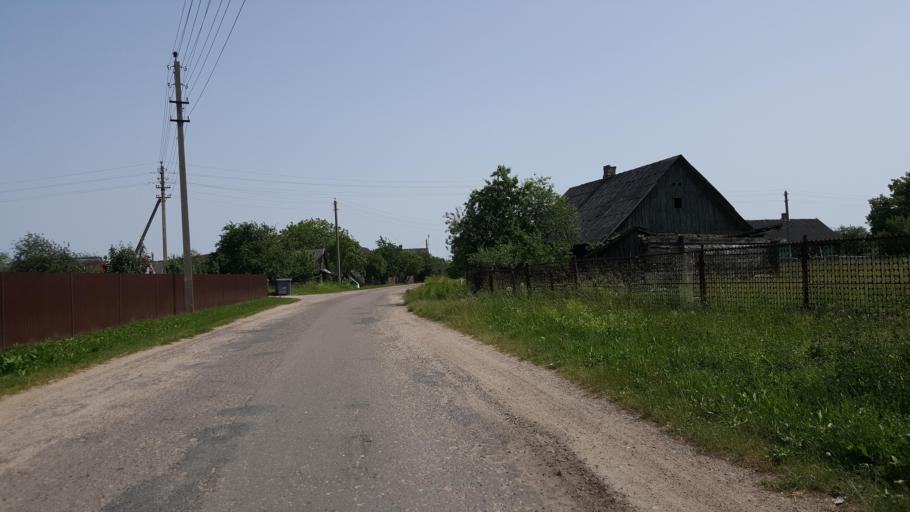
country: BY
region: Brest
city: Kamyanyets
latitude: 52.4068
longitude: 23.7965
